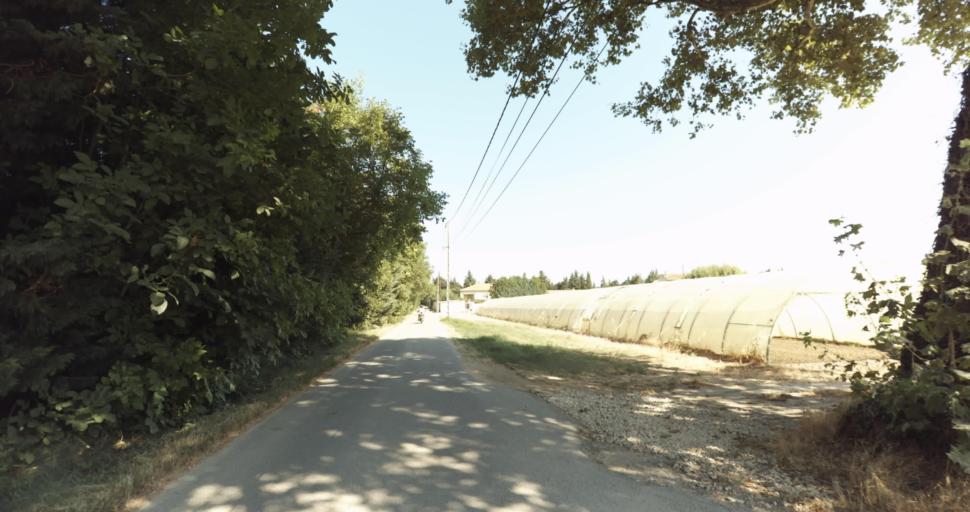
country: FR
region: Provence-Alpes-Cote d'Azur
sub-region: Departement du Vaucluse
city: Althen-des-Paluds
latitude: 44.0109
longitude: 4.9808
